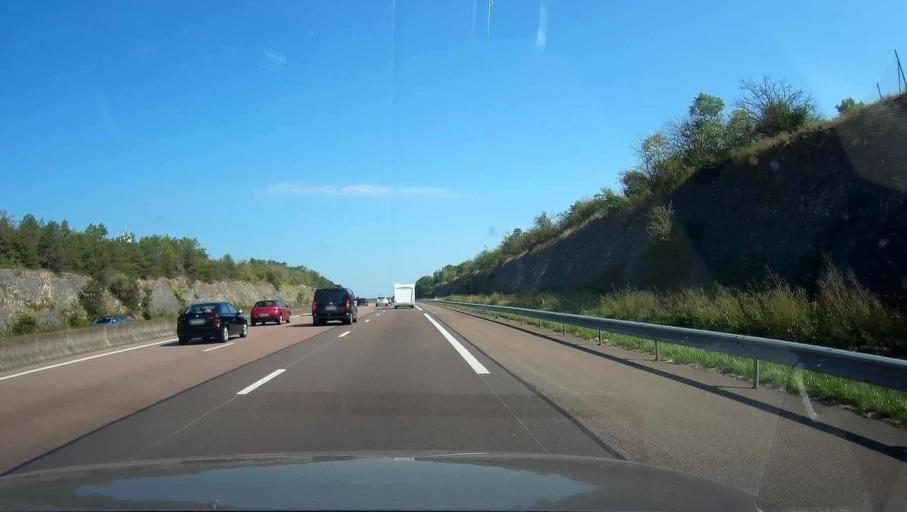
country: FR
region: Bourgogne
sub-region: Departement de la Cote-d'Or
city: Selongey
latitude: 47.5234
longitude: 5.1986
